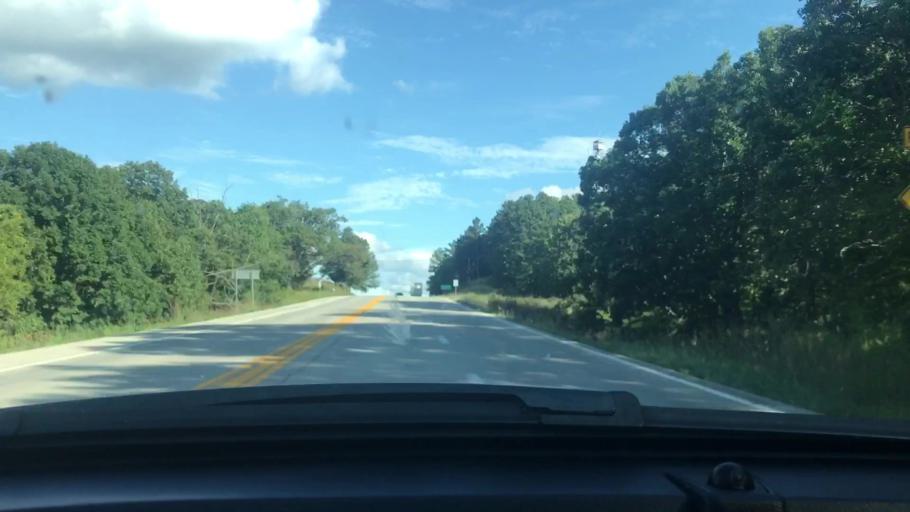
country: US
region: Missouri
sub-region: Howell County
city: West Plains
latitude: 36.6506
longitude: -91.6881
